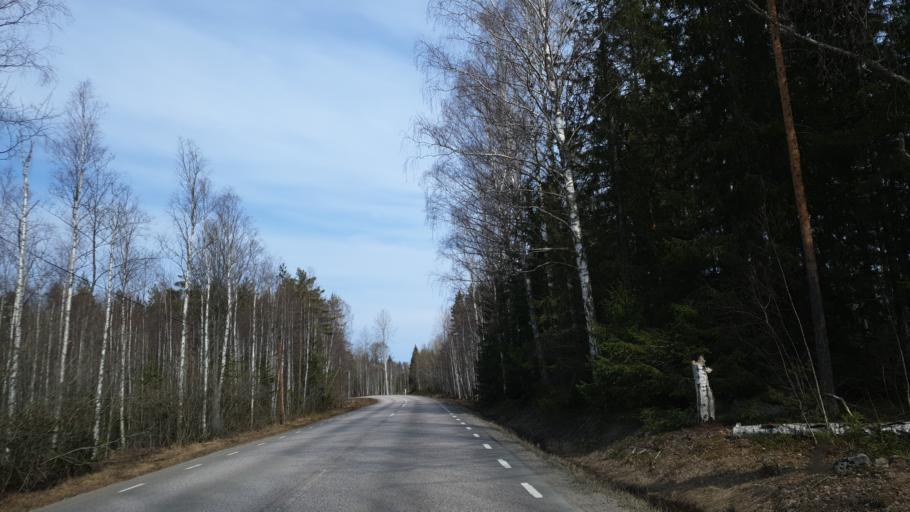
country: SE
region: Gaevleborg
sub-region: Gavle Kommun
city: Norrsundet
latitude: 60.9639
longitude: 17.0443
